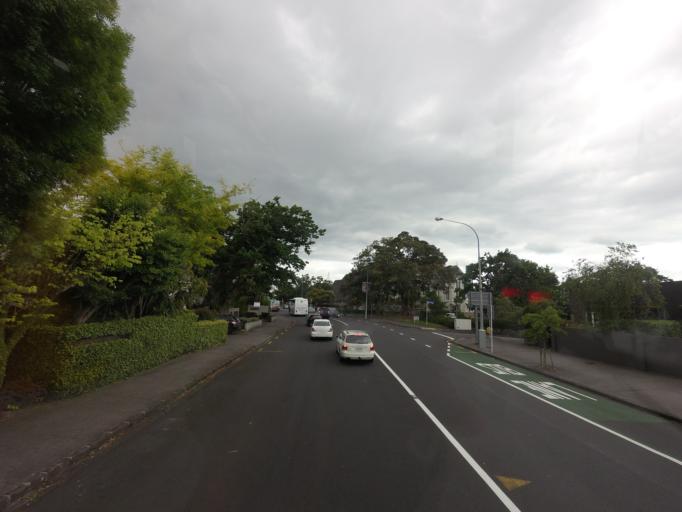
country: NZ
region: Auckland
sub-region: Auckland
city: Auckland
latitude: -36.8608
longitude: 174.7823
